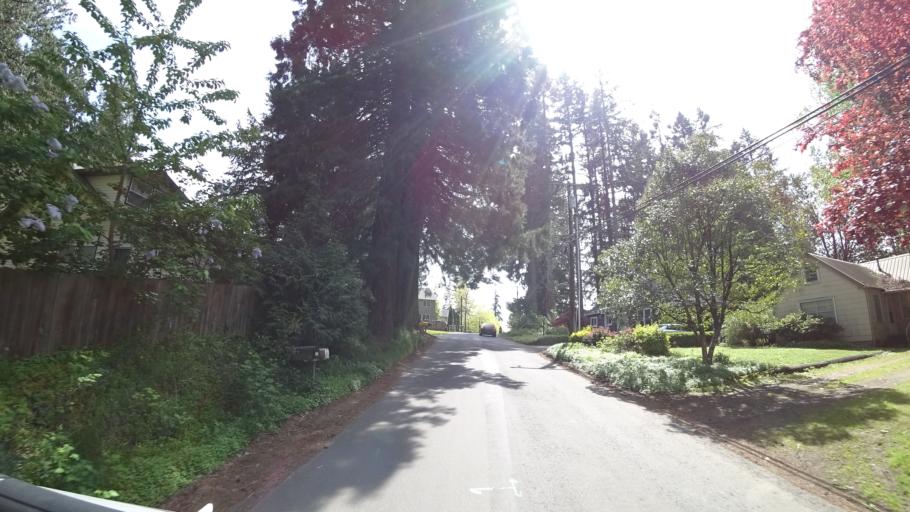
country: US
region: Oregon
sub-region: Washington County
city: Hillsboro
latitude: 45.5236
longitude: -122.9351
